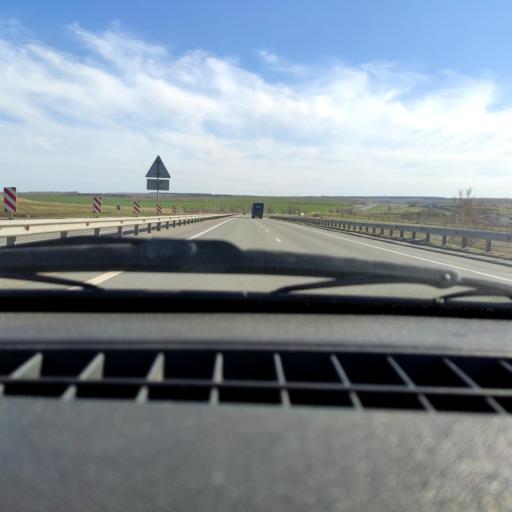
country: RU
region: Bashkortostan
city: Tolbazy
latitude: 54.0757
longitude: 55.8990
